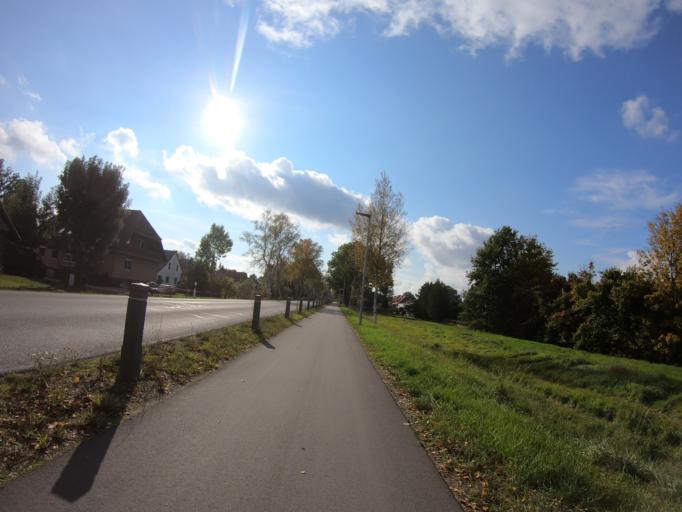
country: DE
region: Lower Saxony
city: Sassenburg
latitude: 52.5308
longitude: 10.5984
